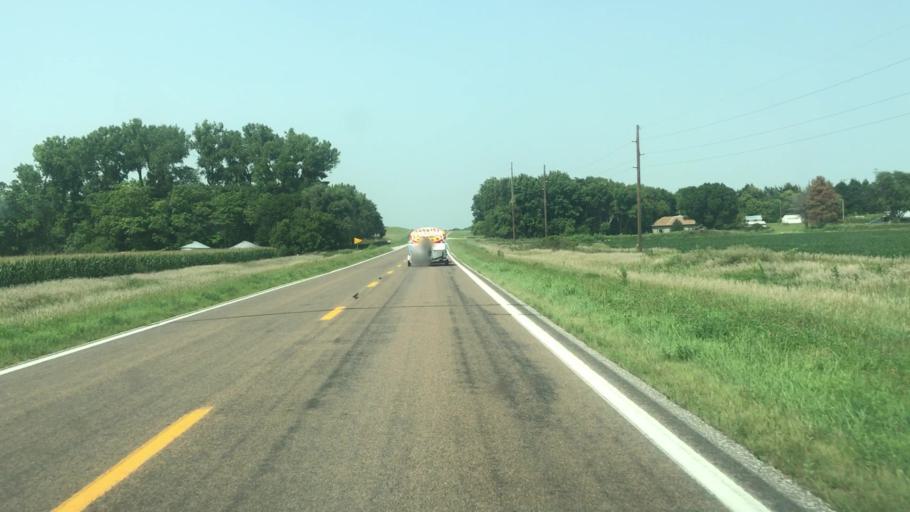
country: US
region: Nebraska
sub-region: Sherman County
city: Loup City
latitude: 41.2471
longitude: -98.9389
